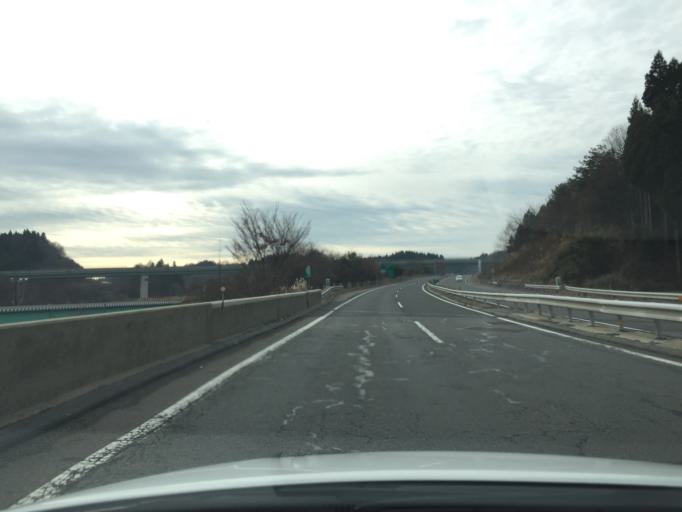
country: JP
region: Fukushima
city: Funehikimachi-funehiki
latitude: 37.2982
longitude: 140.6151
